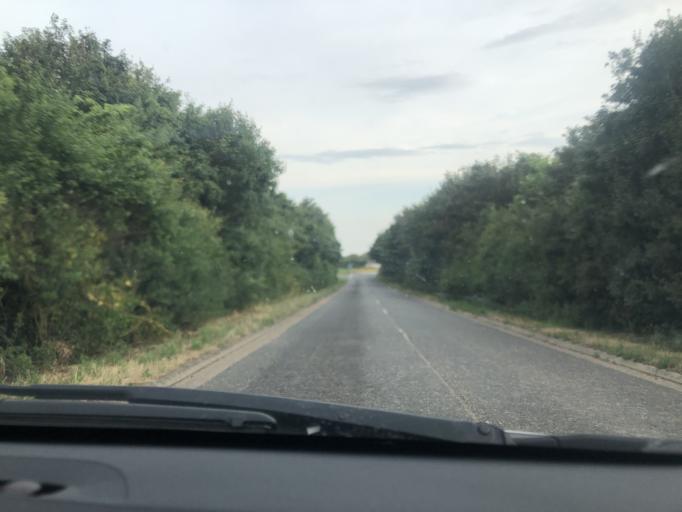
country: GB
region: England
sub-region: Kent
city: Herne Bay
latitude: 51.3595
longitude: 1.1693
